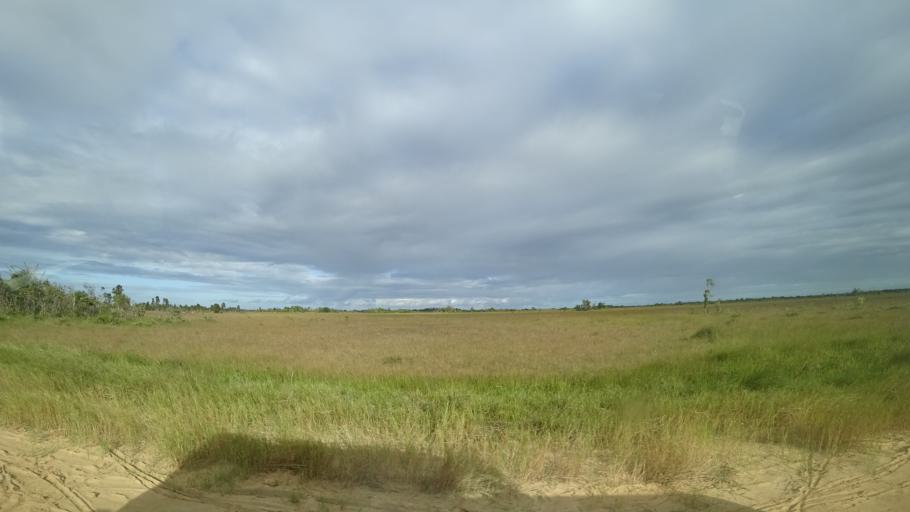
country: MZ
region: Sofala
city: Beira
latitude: -19.6929
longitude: 35.0383
